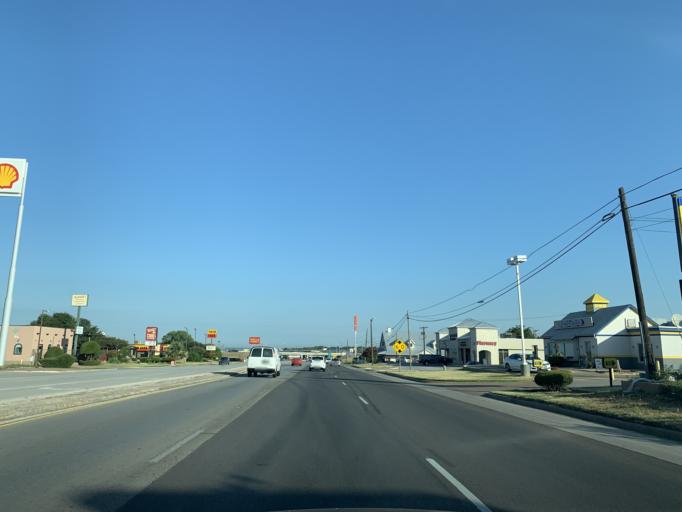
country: US
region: Texas
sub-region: Tarrant County
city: Sansom Park
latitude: 32.8057
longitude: -97.4140
